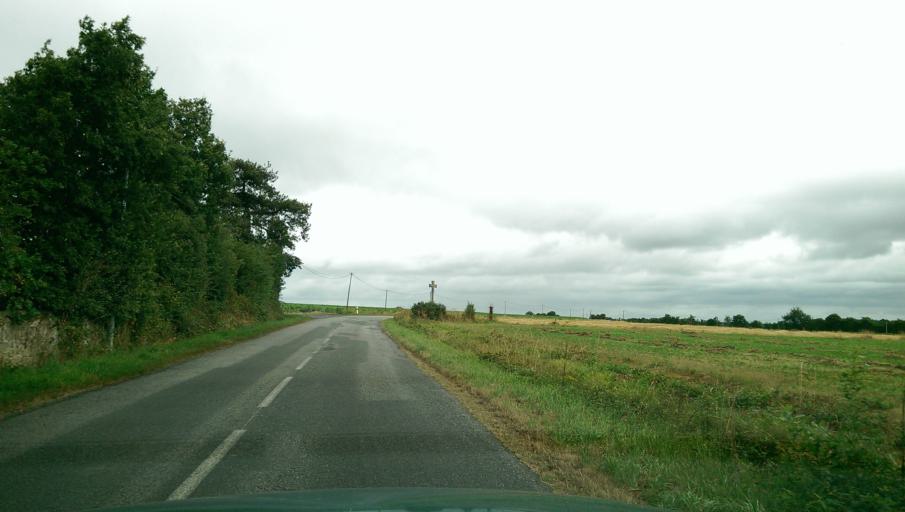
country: FR
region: Pays de la Loire
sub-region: Departement de la Loire-Atlantique
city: Remouille
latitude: 47.0365
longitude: -1.3993
